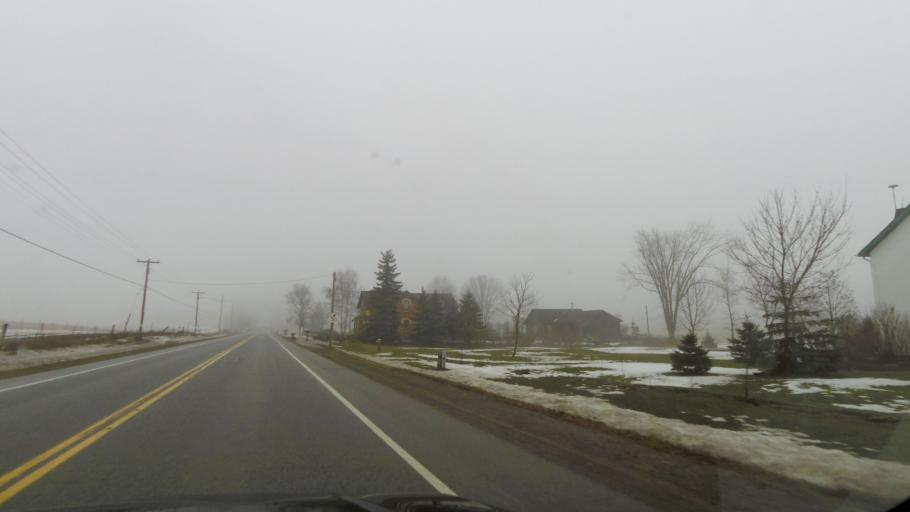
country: CA
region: Ontario
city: Brampton
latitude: 43.8542
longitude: -79.8558
